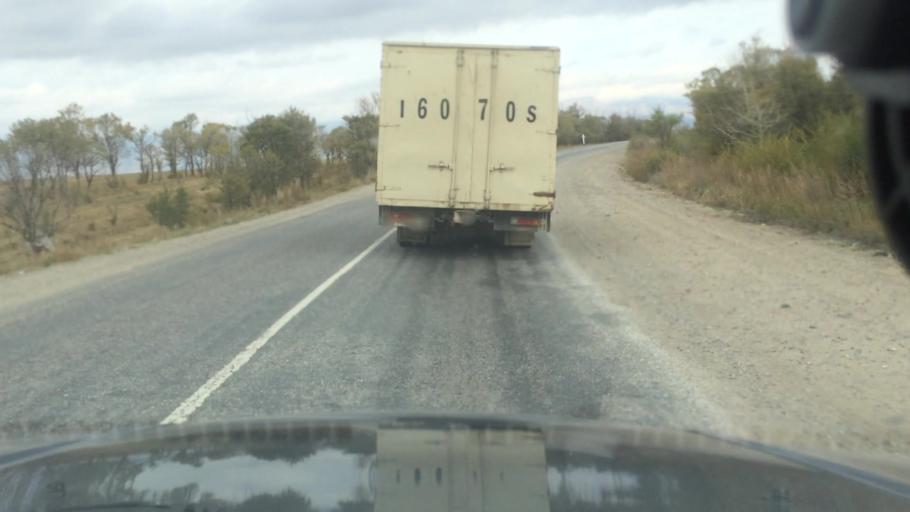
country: KG
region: Ysyk-Koel
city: Tyup
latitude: 42.6678
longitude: 78.3489
